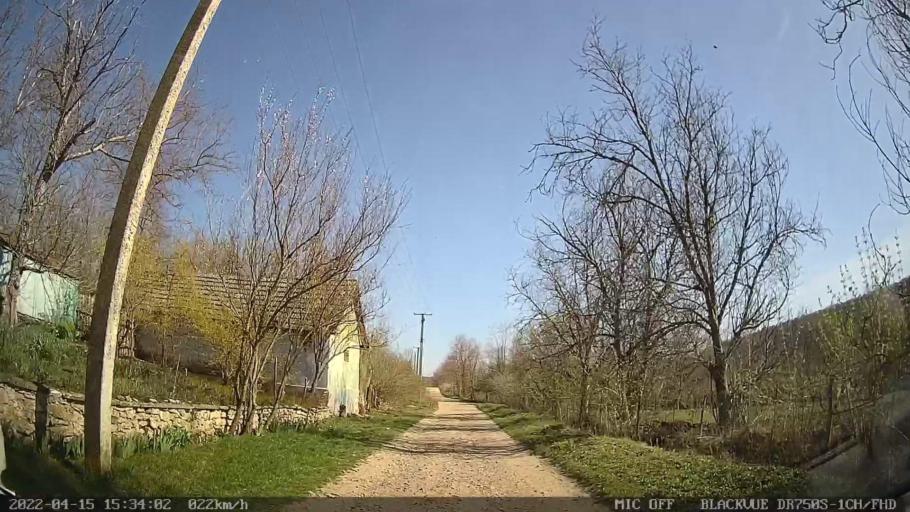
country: MD
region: Raionul Ocnita
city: Otaci
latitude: 48.3483
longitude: 27.9256
